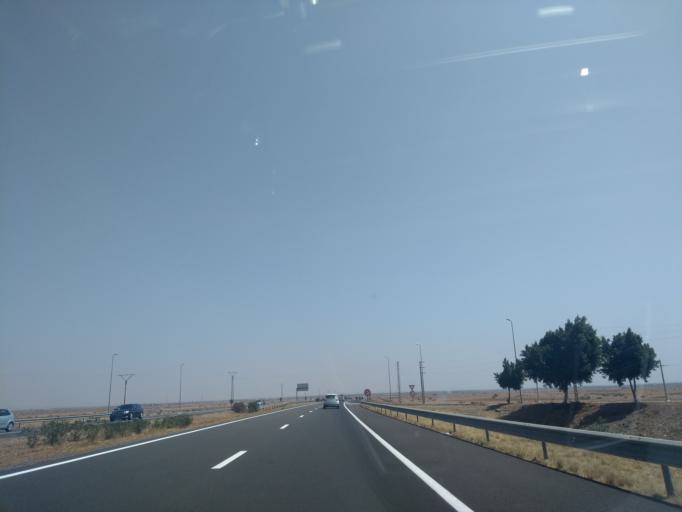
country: MA
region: Marrakech-Tensift-Al Haouz
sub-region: Kelaa-Des-Sraghna
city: Sidi Bou Othmane
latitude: 31.9202
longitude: -8.0240
